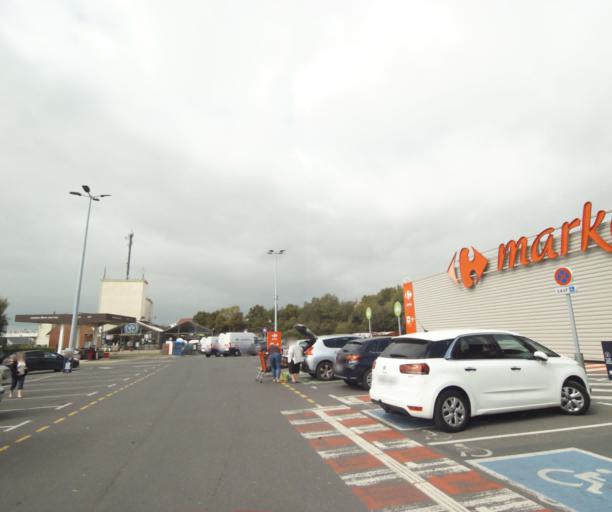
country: FR
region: Nord-Pas-de-Calais
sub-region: Departement du Pas-de-Calais
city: Etaples
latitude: 50.5156
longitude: 1.6457
